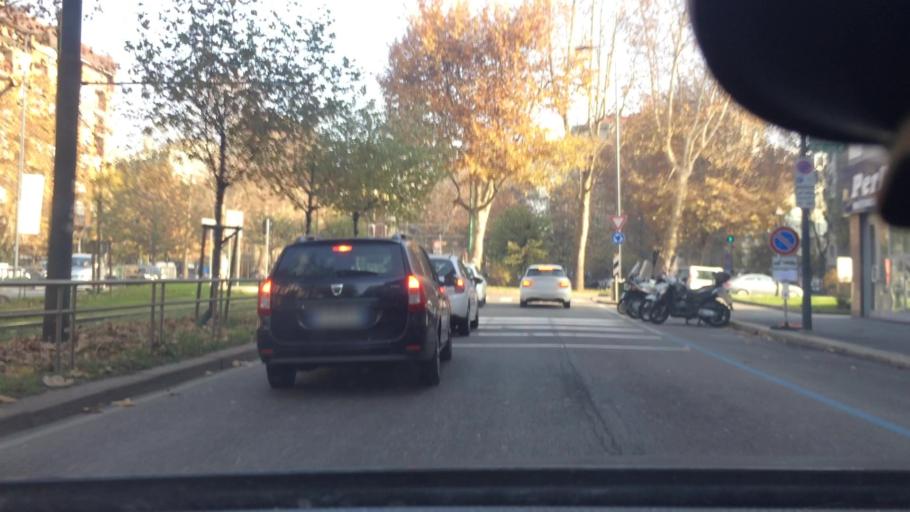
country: IT
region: Lombardy
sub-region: Citta metropolitana di Milano
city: Milano
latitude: 45.4877
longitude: 9.1602
